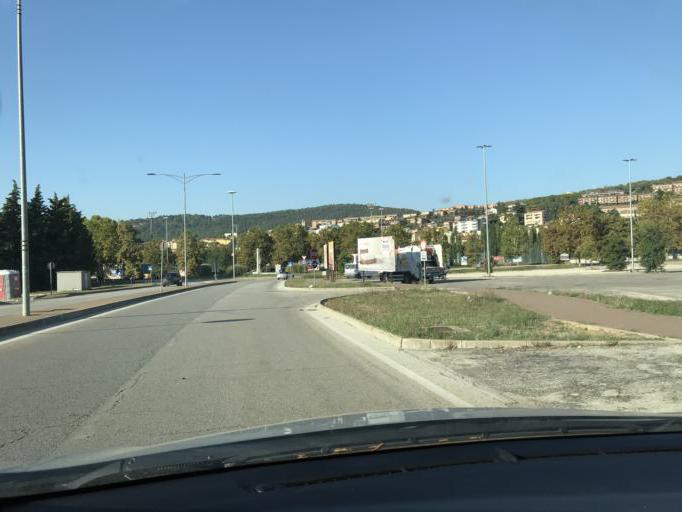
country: IT
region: Umbria
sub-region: Provincia di Perugia
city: Perugia
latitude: 43.1099
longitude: 12.3590
